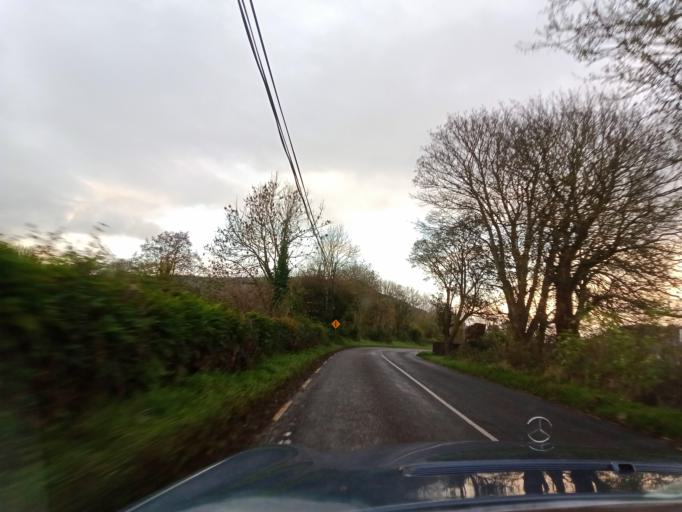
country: IE
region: Munster
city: Carrick-on-Suir
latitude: 52.3907
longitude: -7.3905
